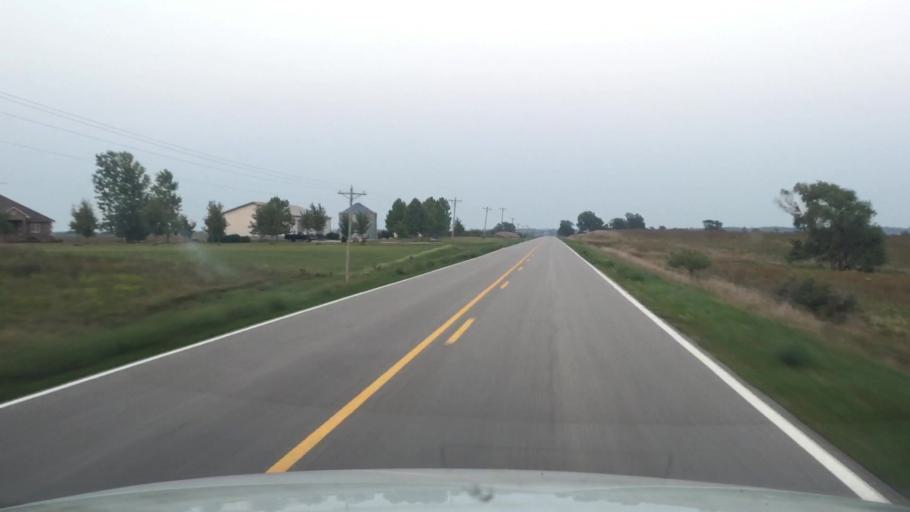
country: US
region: Iowa
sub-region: Warren County
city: Indianola
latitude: 41.1907
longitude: -93.5754
